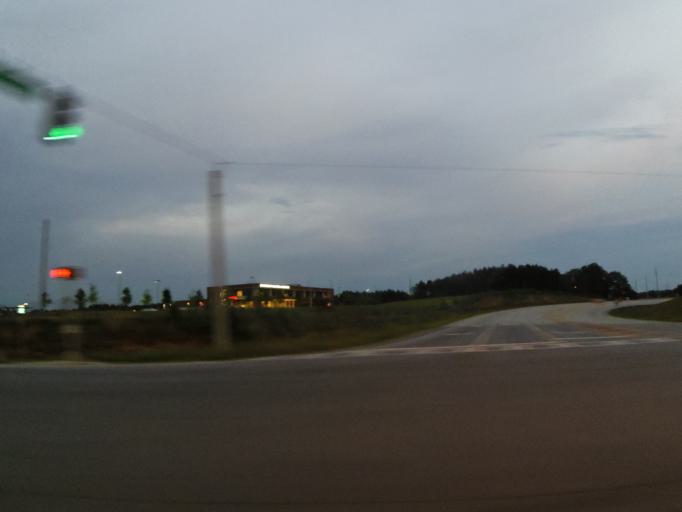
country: US
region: Georgia
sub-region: McDuffie County
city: Thomson
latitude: 33.5225
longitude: -82.5044
